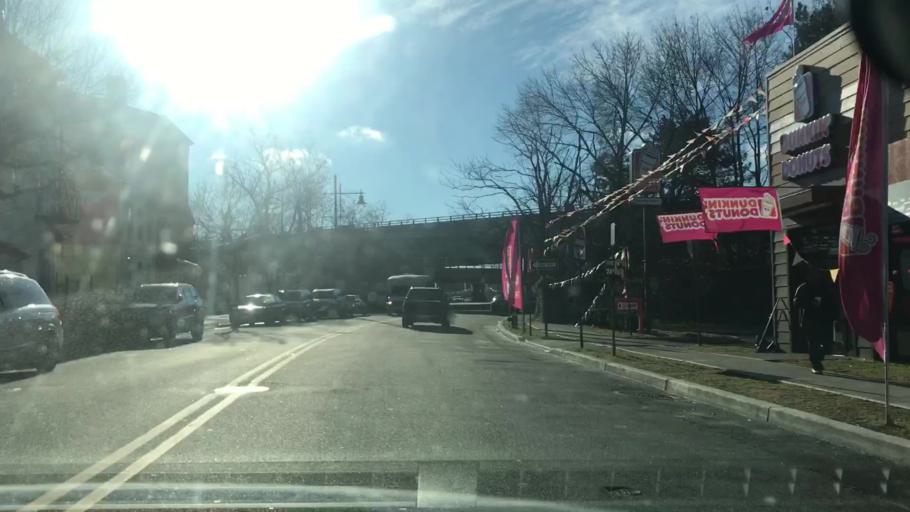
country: US
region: New Jersey
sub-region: Passaic County
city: Paterson
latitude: 40.9089
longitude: -74.1711
